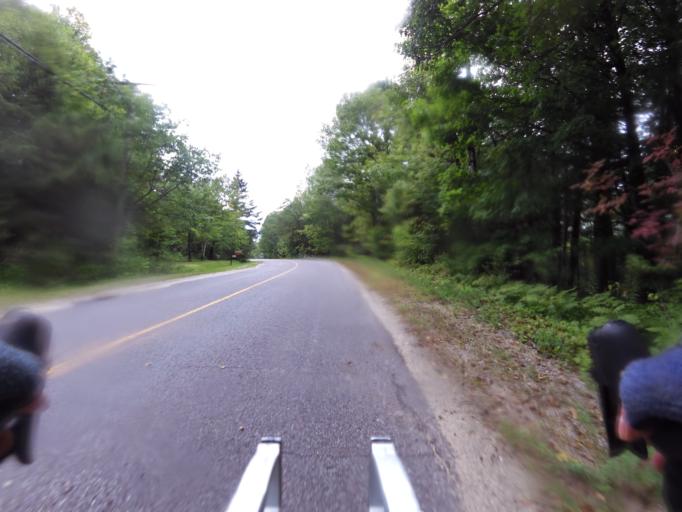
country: CA
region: Quebec
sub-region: Outaouais
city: Wakefield
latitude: 45.6452
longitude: -75.9122
